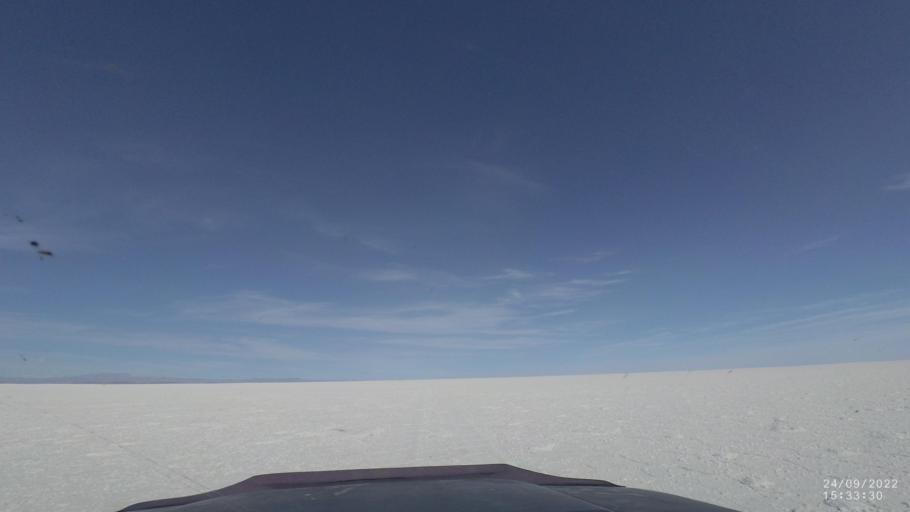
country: BO
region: Potosi
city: Colchani
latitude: -20.1163
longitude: -67.2705
